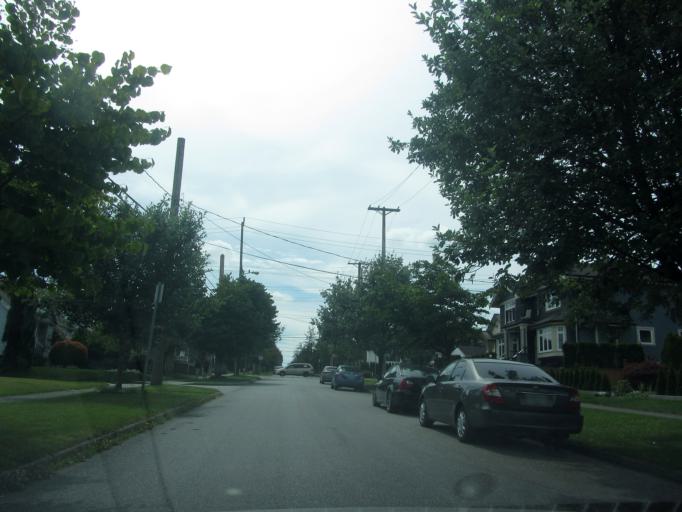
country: CA
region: British Columbia
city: New Westminster
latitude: 49.2179
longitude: -122.9221
